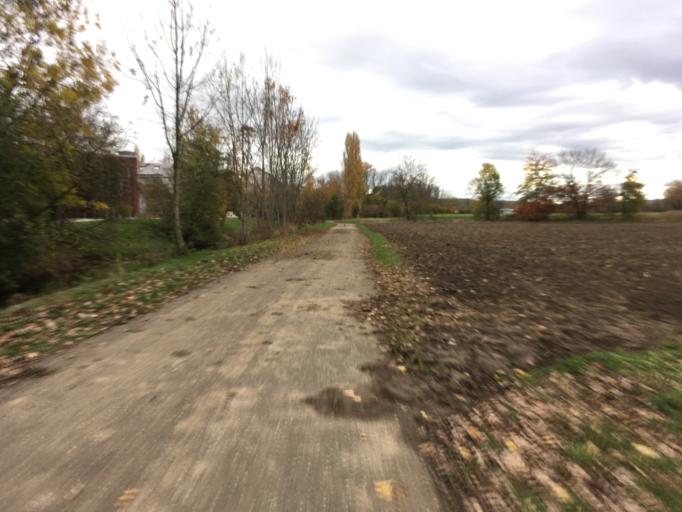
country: DE
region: Baden-Wuerttemberg
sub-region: Freiburg Region
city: Botzingen
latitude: 48.0672
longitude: 7.7246
